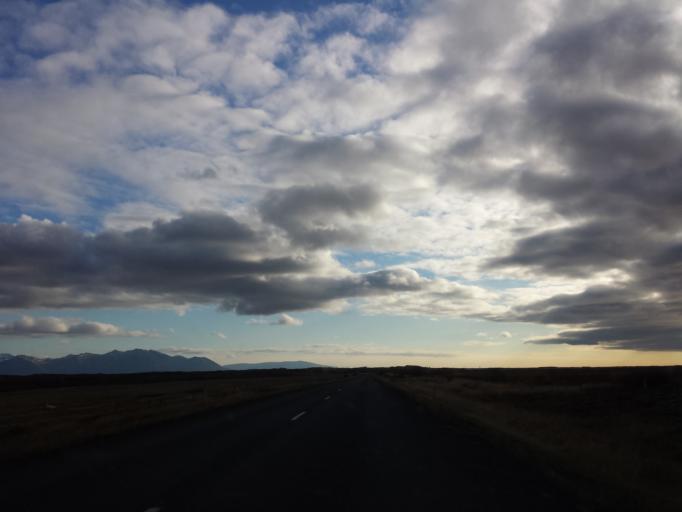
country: IS
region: West
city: Borgarnes
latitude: 64.6633
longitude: -22.0698
